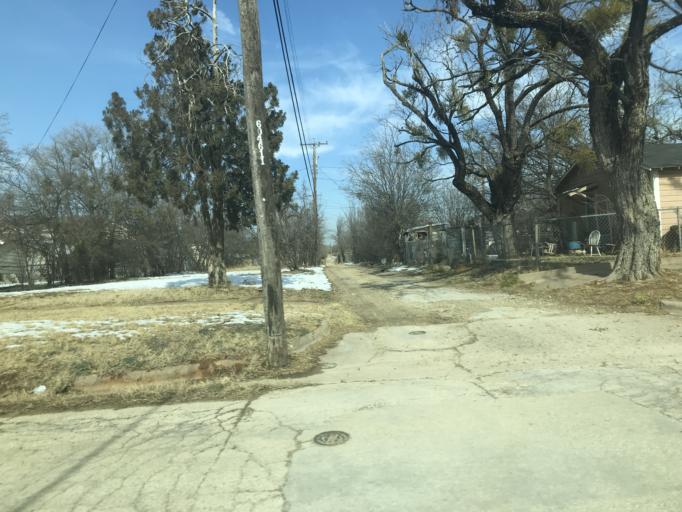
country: US
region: Texas
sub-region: Taylor County
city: Abilene
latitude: 32.4571
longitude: -99.7291
